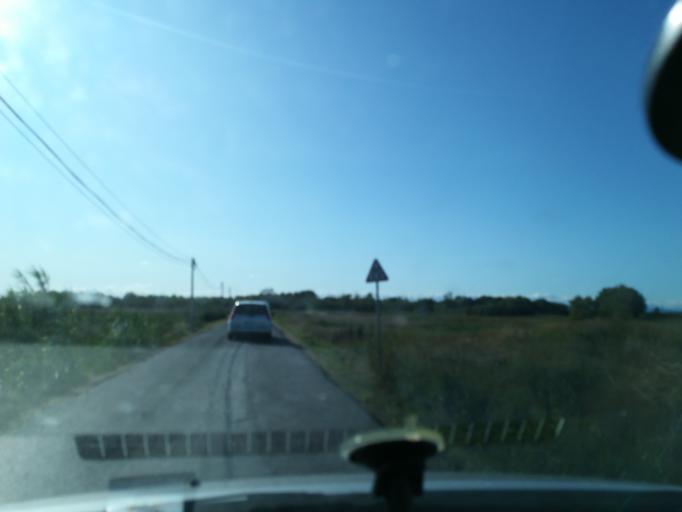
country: FR
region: Languedoc-Roussillon
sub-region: Departement de l'Herault
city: Portiragnes
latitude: 43.2880
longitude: 3.3688
